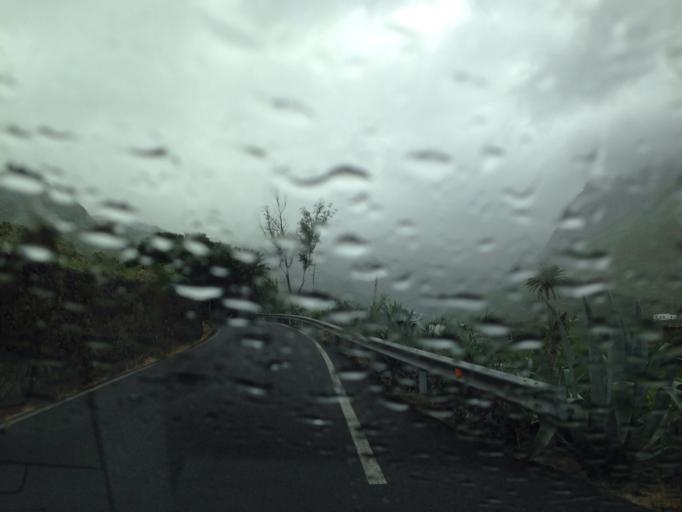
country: ES
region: Canary Islands
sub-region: Provincia de Las Palmas
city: Agaete
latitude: 28.0962
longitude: -15.6882
